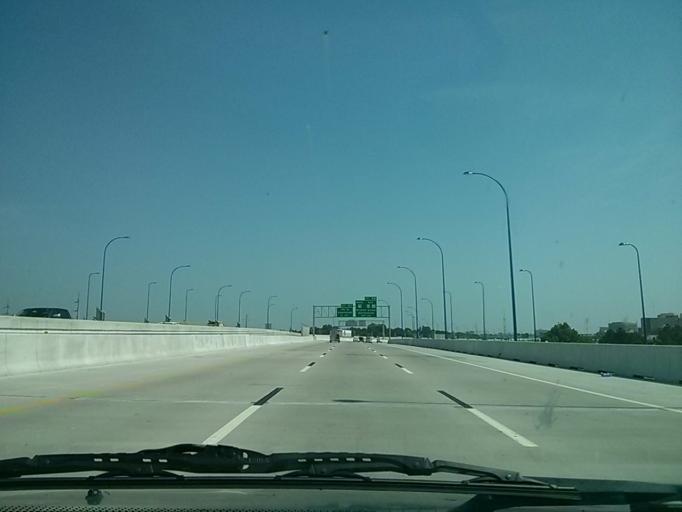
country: US
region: Oklahoma
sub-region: Tulsa County
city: Tulsa
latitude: 36.1382
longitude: -96.0075
